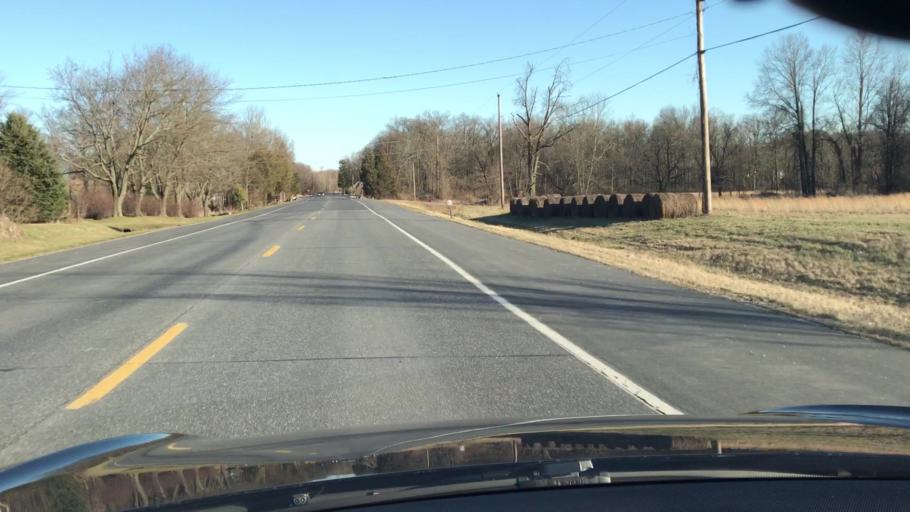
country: US
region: Pennsylvania
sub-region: York County
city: Valley Green
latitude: 40.1426
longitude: -76.8731
